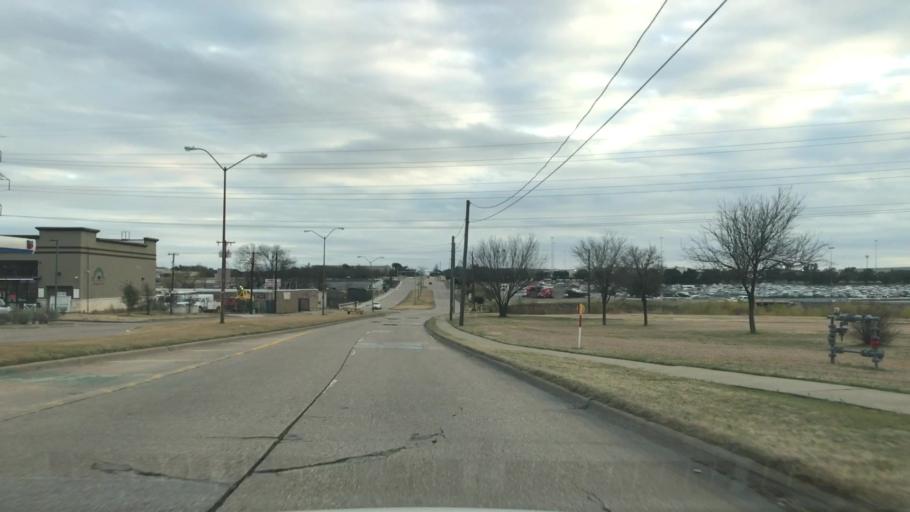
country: US
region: Texas
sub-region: Dallas County
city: Cockrell Hill
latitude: 32.7107
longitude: -96.9087
